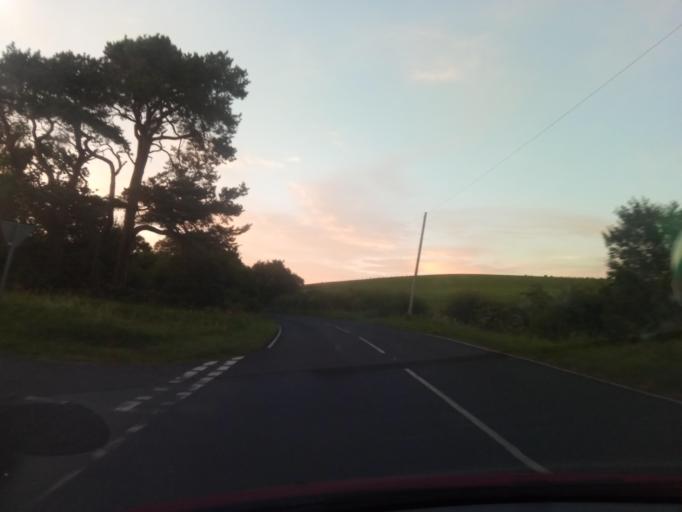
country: GB
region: England
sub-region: Northumberland
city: Bardon Mill
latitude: 54.9409
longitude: -2.2853
